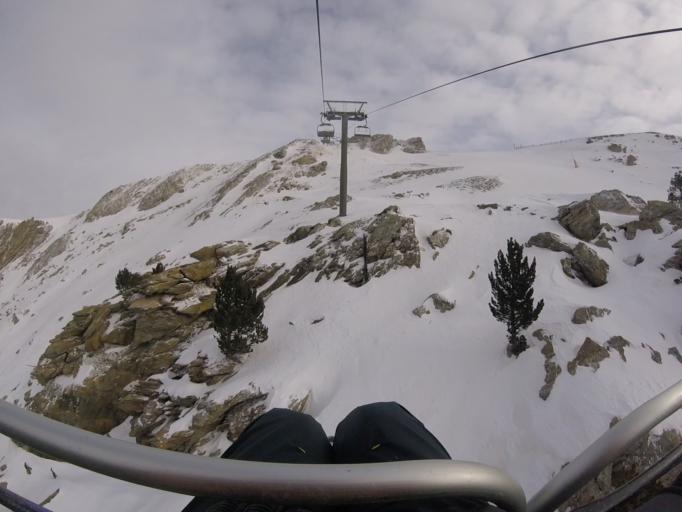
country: AD
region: Canillo
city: Canillo
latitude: 42.5528
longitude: 1.6257
